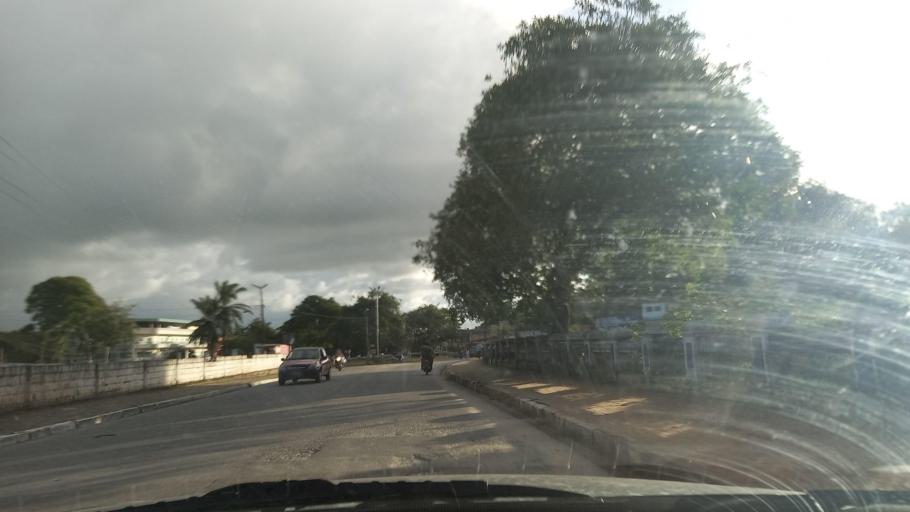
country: BR
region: Pernambuco
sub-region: Palmares
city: Palmares
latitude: -8.6813
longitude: -35.5849
